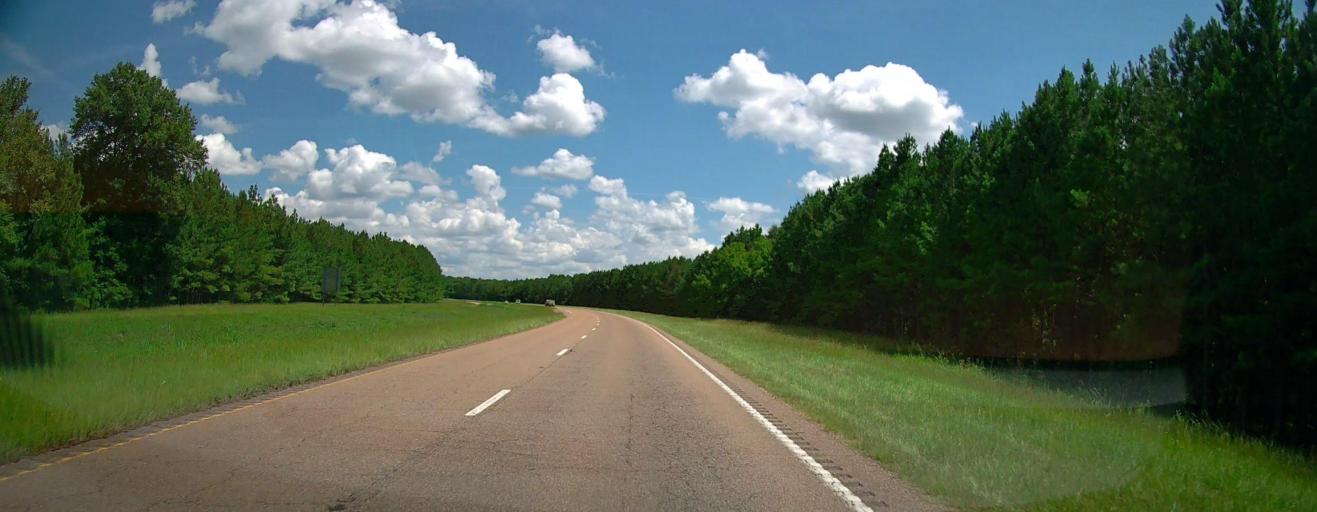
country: US
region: Mississippi
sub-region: Monroe County
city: Aberdeen
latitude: 33.8227
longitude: -88.5837
